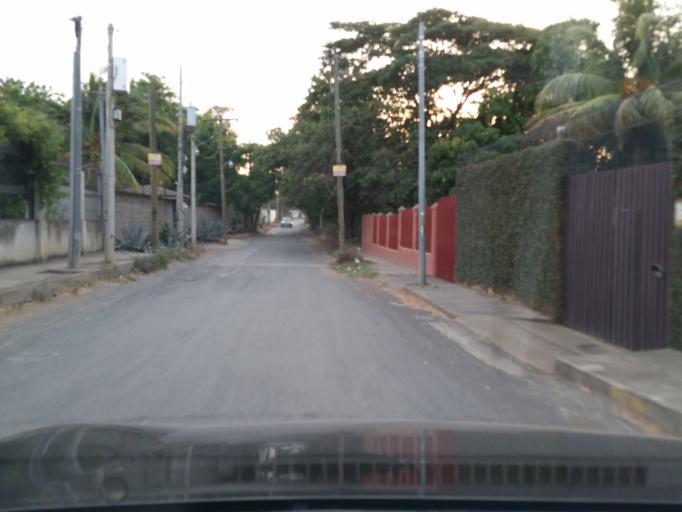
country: NI
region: Managua
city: Managua
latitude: 12.0884
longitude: -86.2231
